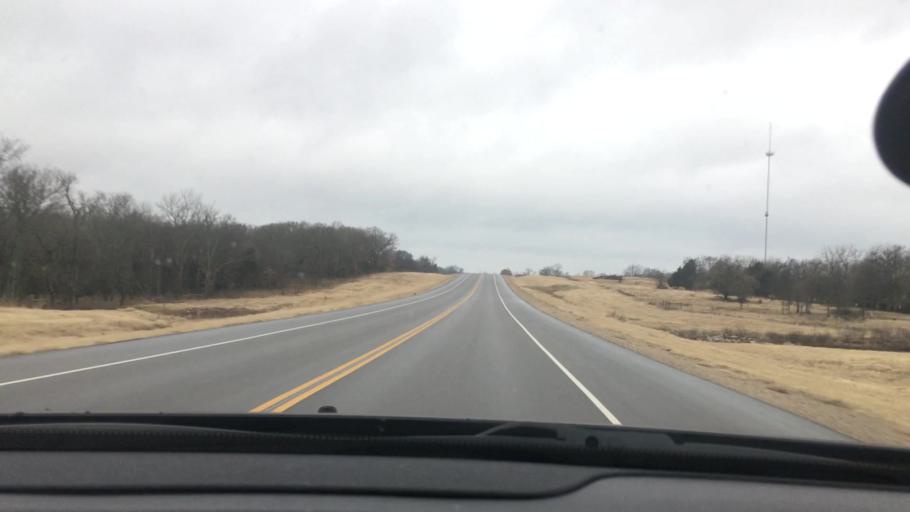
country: US
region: Oklahoma
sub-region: Johnston County
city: Tishomingo
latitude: 34.3239
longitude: -96.6648
